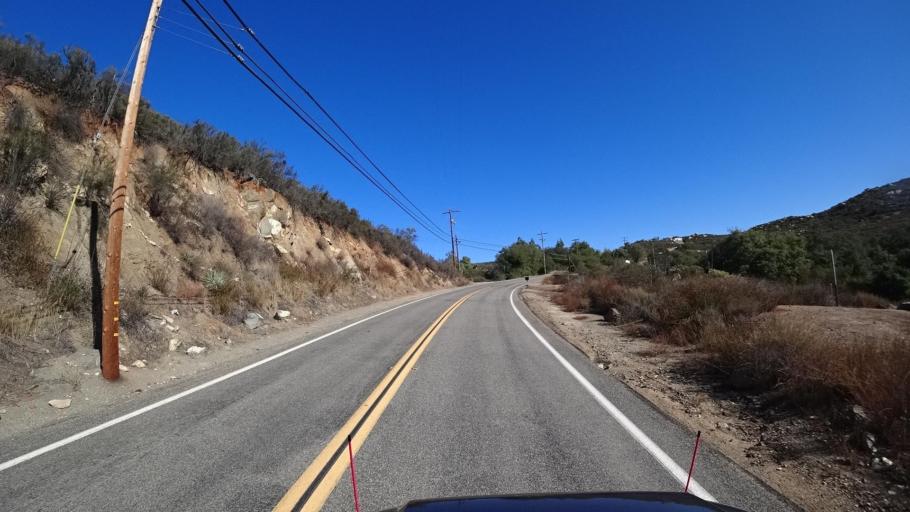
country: US
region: California
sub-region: San Diego County
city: Jamul
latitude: 32.6998
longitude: -116.7469
